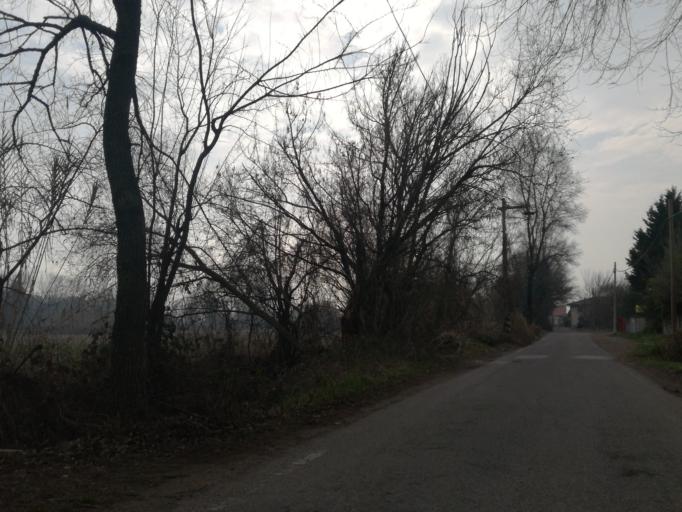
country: IT
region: Lombardy
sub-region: Citta metropolitana di Milano
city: Romano Banco
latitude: 45.4374
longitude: 9.1376
